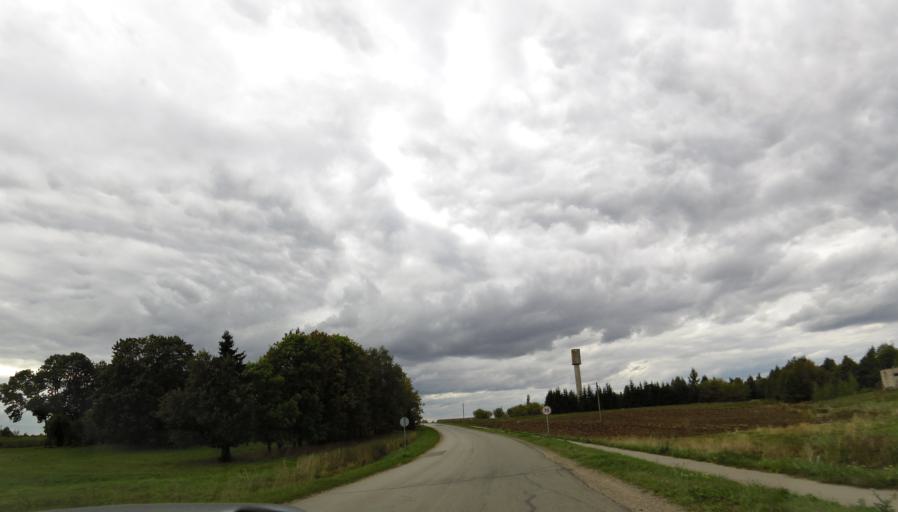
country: LT
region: Panevezys
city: Pasvalys
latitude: 56.0793
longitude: 24.3620
